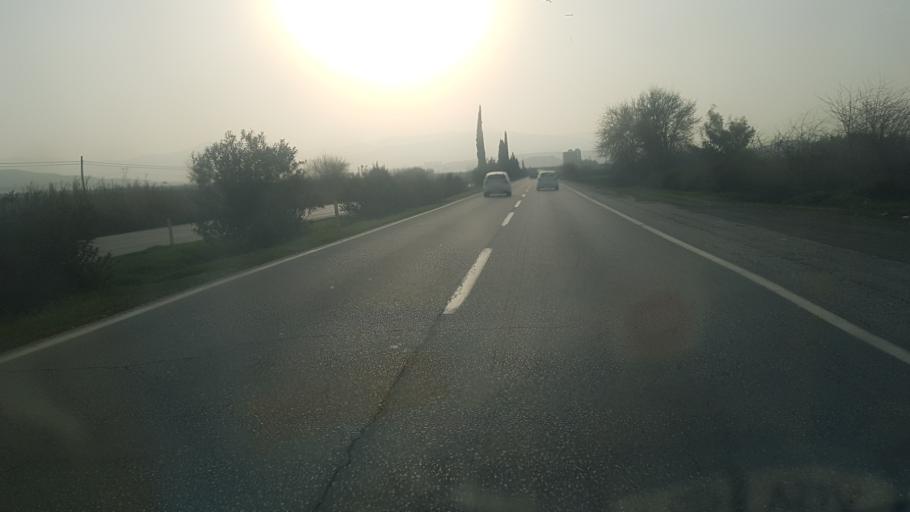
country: TR
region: Osmaniye
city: Toprakkale
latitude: 37.0678
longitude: 36.0982
